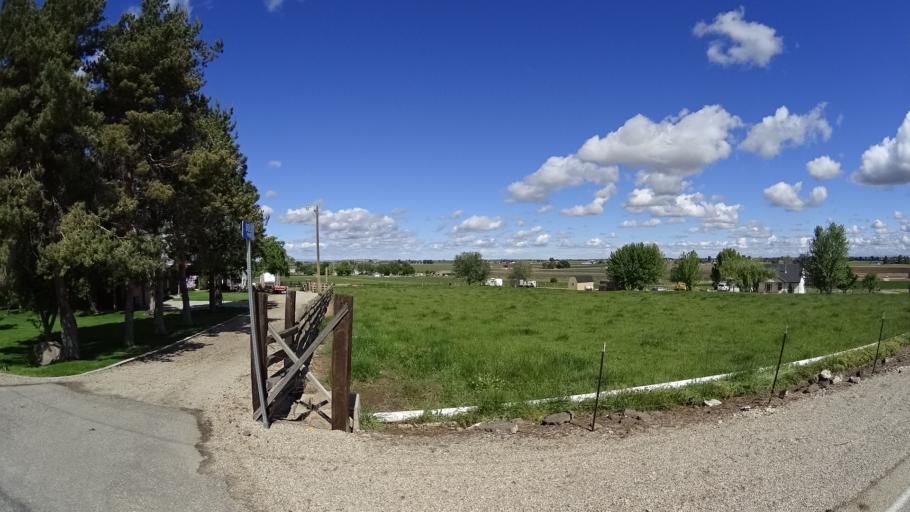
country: US
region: Idaho
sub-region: Ada County
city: Kuna
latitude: 43.4643
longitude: -116.4673
